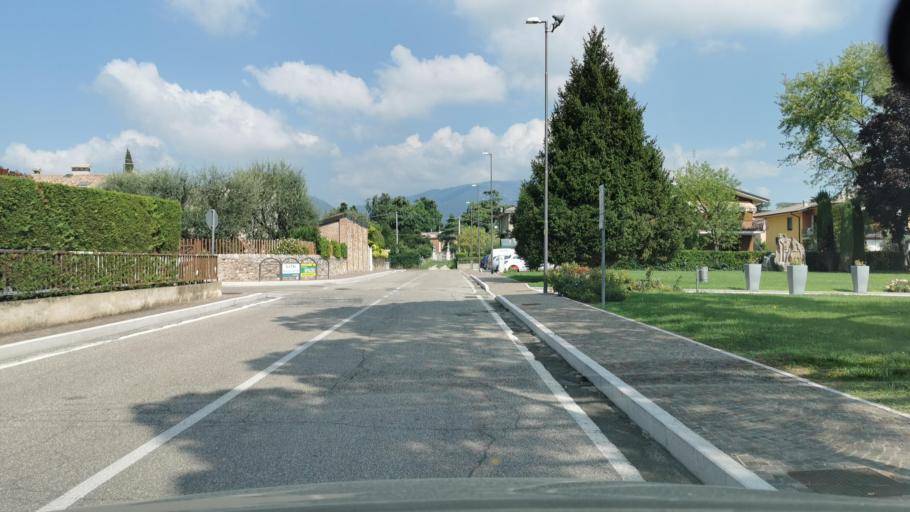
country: IT
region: Veneto
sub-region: Provincia di Verona
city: Cavajon Veronese
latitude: 45.5517
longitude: 10.7729
